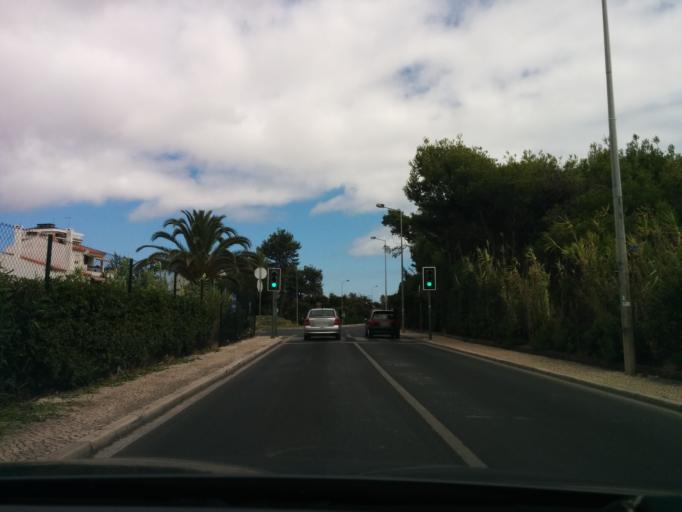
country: PT
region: Lisbon
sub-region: Cascais
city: Estoril
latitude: 38.6994
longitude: -9.3848
